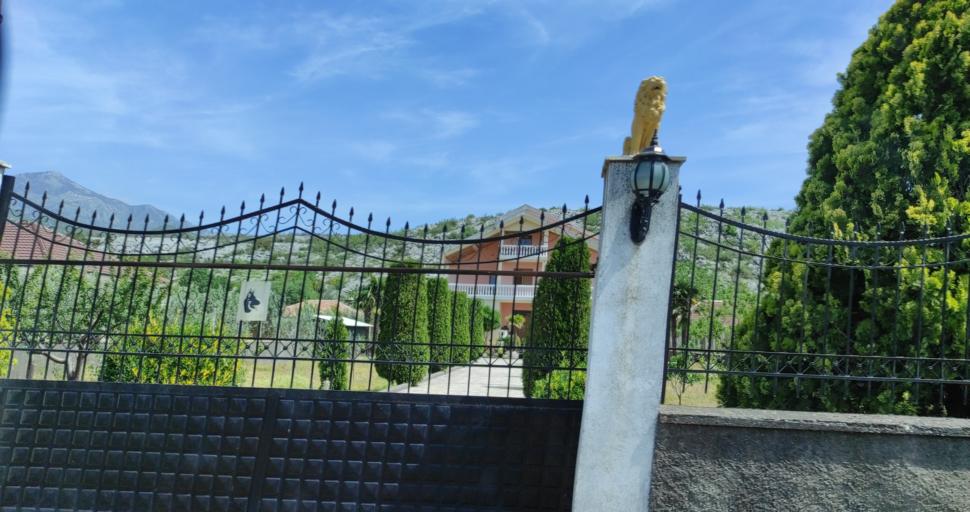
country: AL
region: Shkoder
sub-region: Rrethi i Malesia e Madhe
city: Gruemire
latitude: 42.1247
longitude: 19.5570
